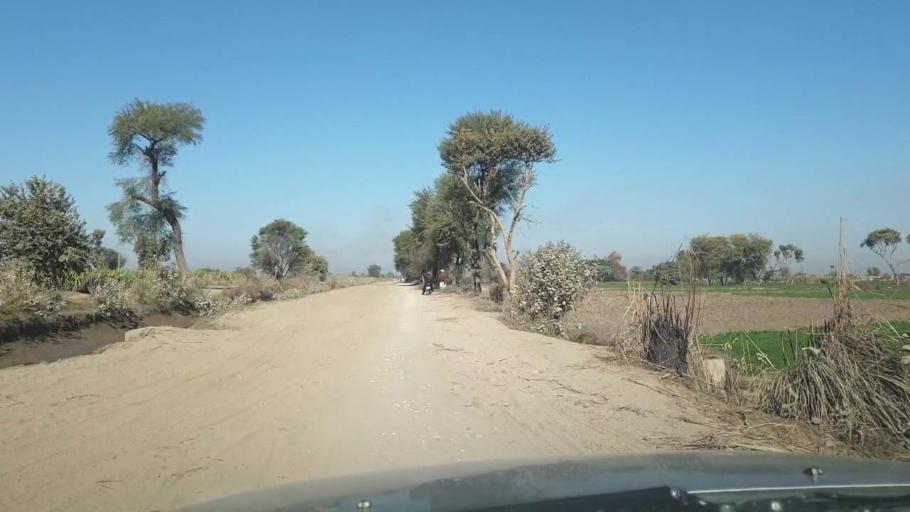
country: PK
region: Sindh
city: Ghotki
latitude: 28.0750
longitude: 69.3473
